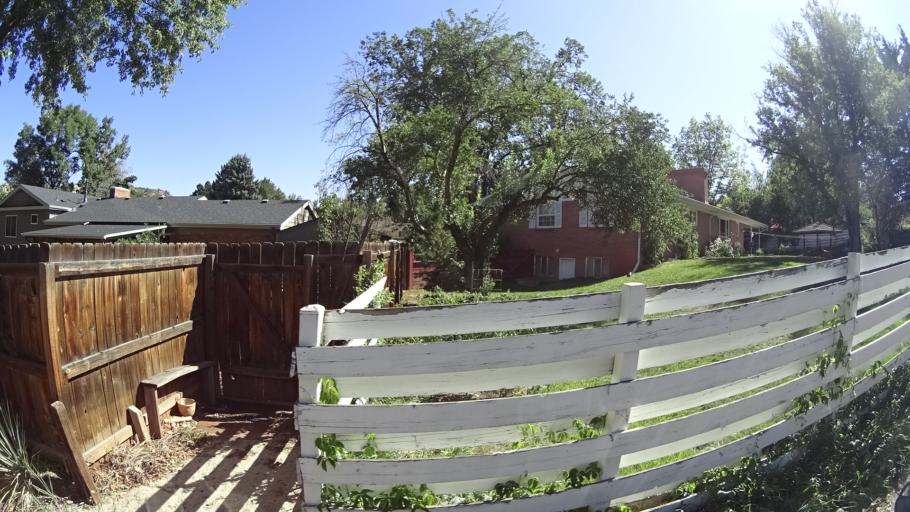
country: US
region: Colorado
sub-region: El Paso County
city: Colorado Springs
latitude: 38.8746
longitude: -104.7854
